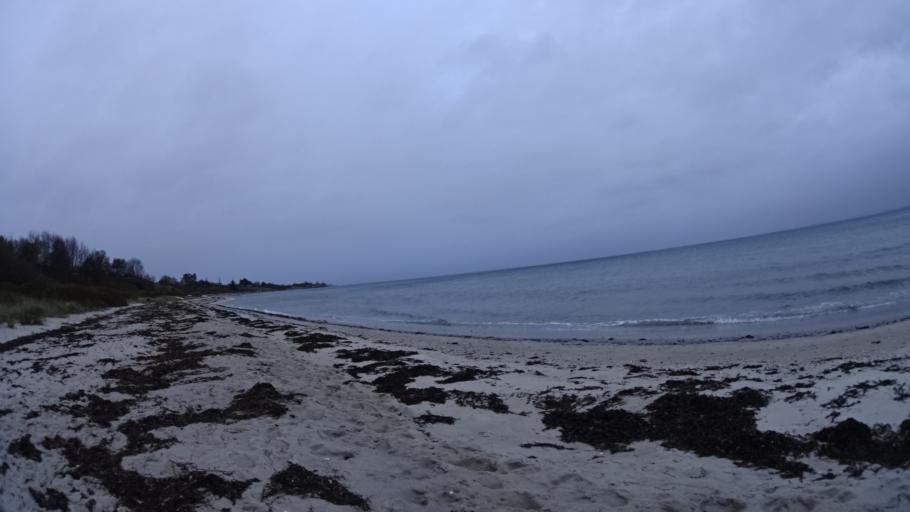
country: DK
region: Central Jutland
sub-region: Arhus Kommune
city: Malling
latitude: 55.9911
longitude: 10.2530
